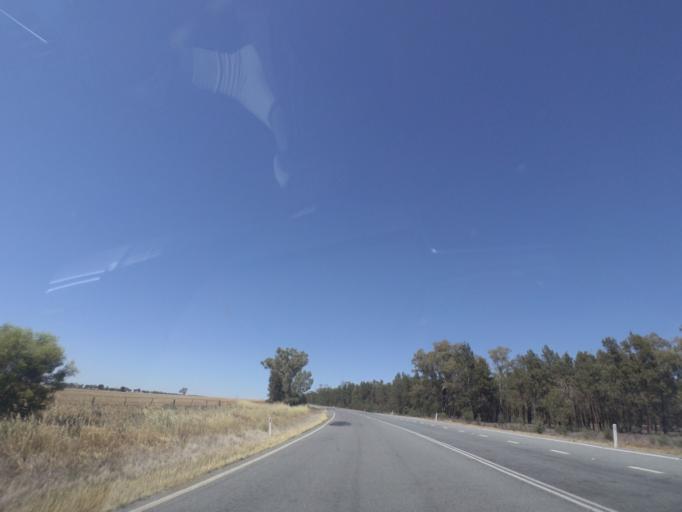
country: AU
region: New South Wales
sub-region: Narrandera
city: Narrandera
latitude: -34.4219
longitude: 146.8451
